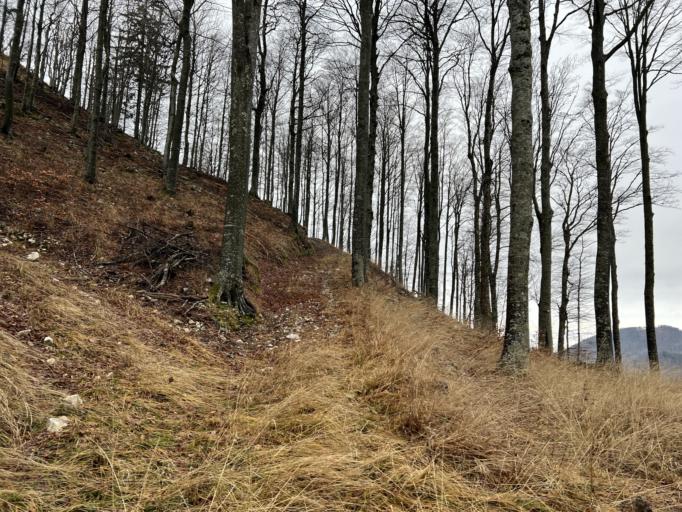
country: SI
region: Nova Gorica
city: Sempas
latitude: 45.9512
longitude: 13.8189
